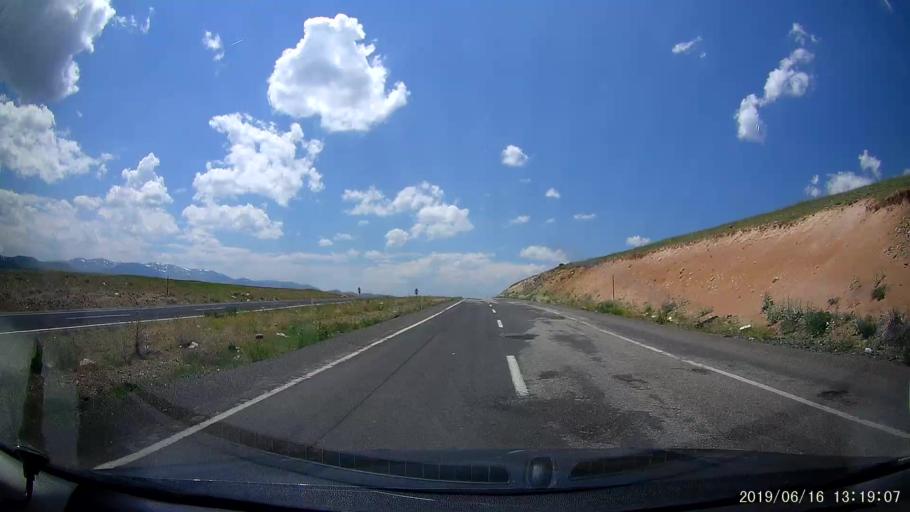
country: TR
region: Agri
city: Taslicay
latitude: 39.6326
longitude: 43.4152
